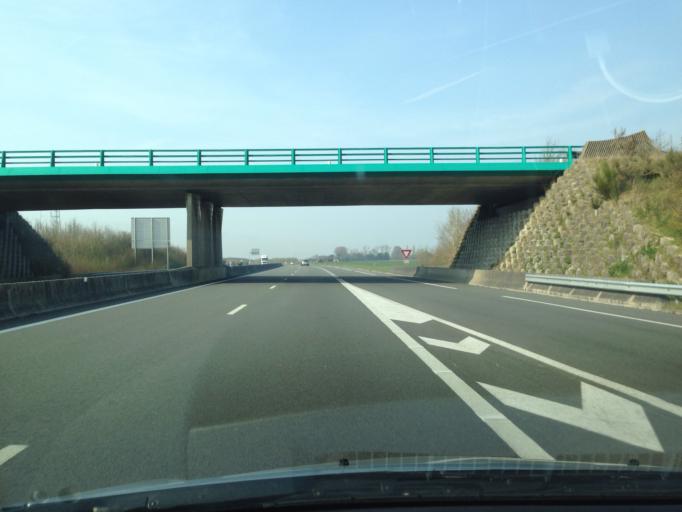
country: FR
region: Picardie
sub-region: Departement de la Somme
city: Nouvion
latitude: 50.2516
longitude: 1.7499
